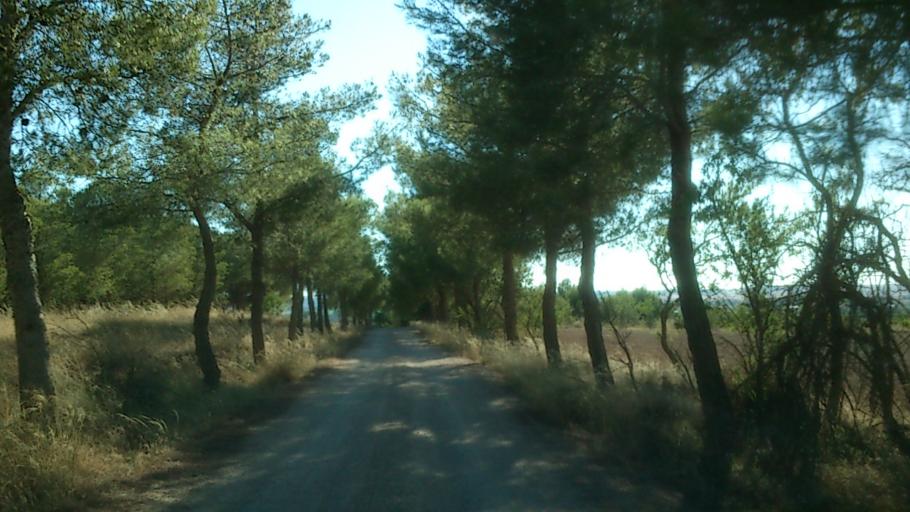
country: ES
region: Aragon
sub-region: Provincia de Zaragoza
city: Villanueva de Gallego
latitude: 41.7665
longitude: -0.7803
